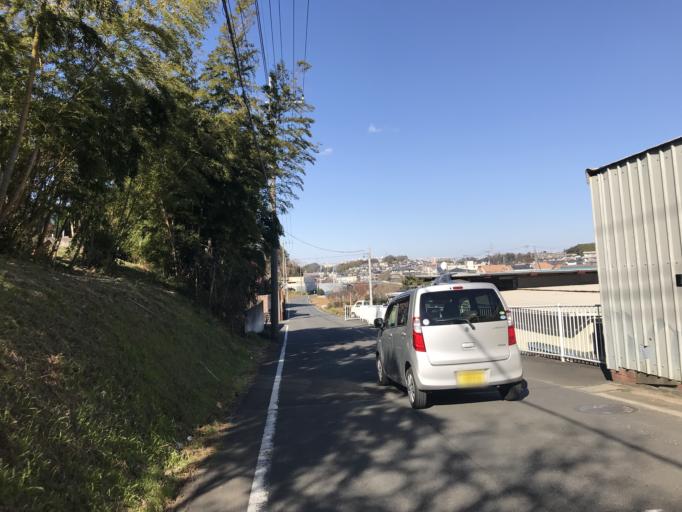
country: JP
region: Tokyo
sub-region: Machida-shi
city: Machida
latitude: 35.5717
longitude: 139.5089
